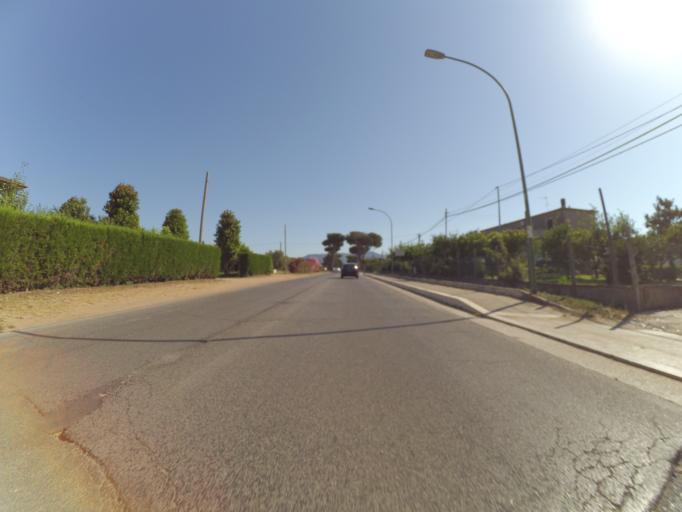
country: IT
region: Latium
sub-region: Provincia di Latina
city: San Felice Circeo
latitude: 41.2810
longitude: 13.1033
